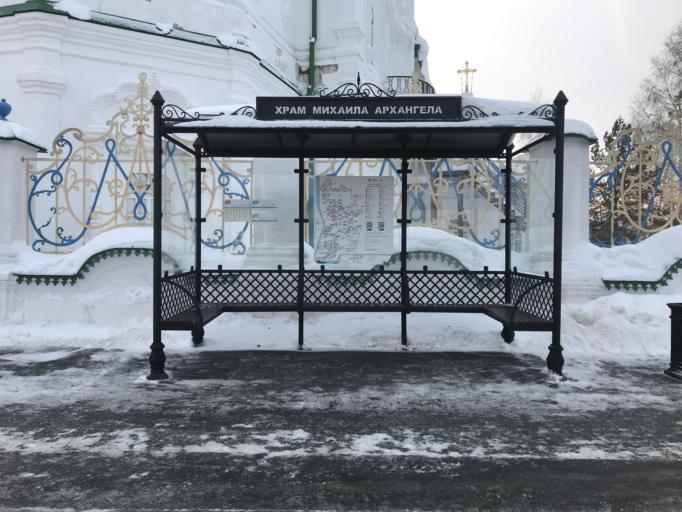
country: RU
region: Tjumen
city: Tobol'sk
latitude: 58.1929
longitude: 68.2501
